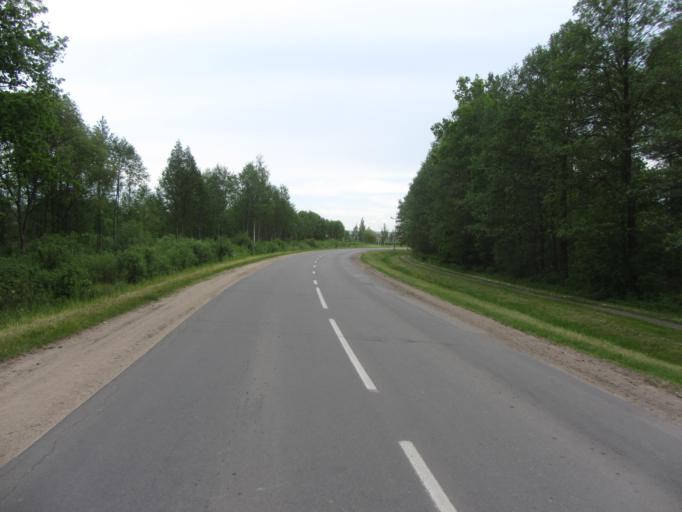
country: LT
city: Kaisiadorys
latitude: 54.8667
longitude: 24.4326
